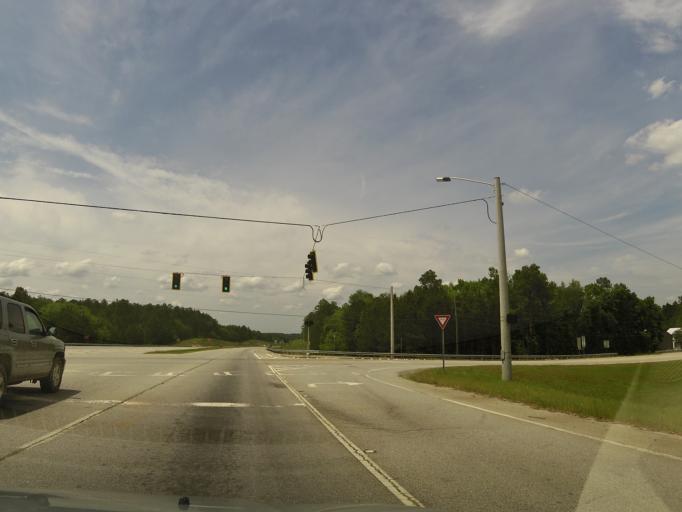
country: US
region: Georgia
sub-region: Emanuel County
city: Swainsboro
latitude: 32.5761
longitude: -82.3587
